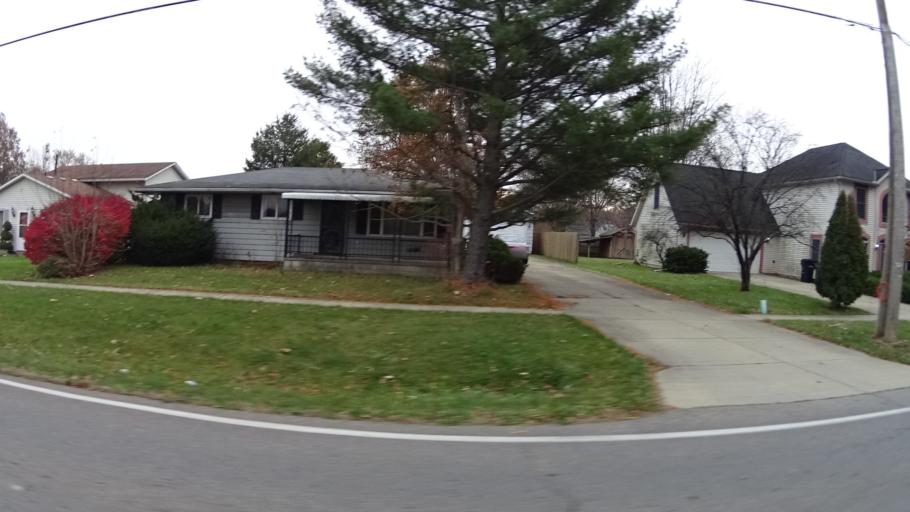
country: US
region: Ohio
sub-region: Lorain County
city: Elyria
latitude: 41.3440
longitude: -82.1076
